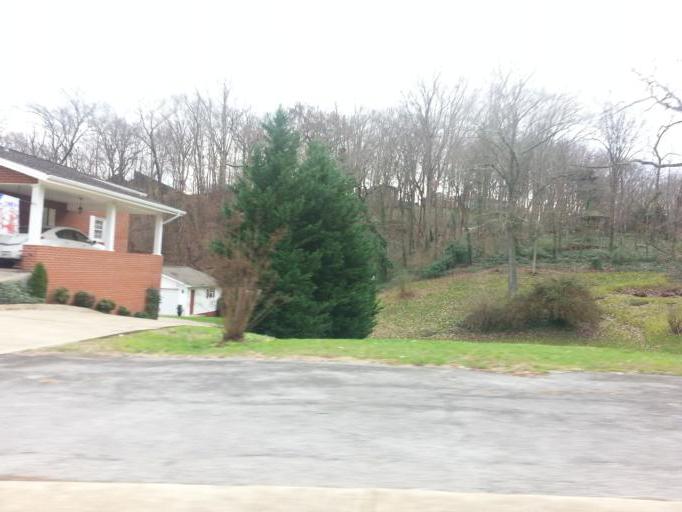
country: US
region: Tennessee
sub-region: Greene County
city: Greeneville
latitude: 36.1588
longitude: -82.8360
